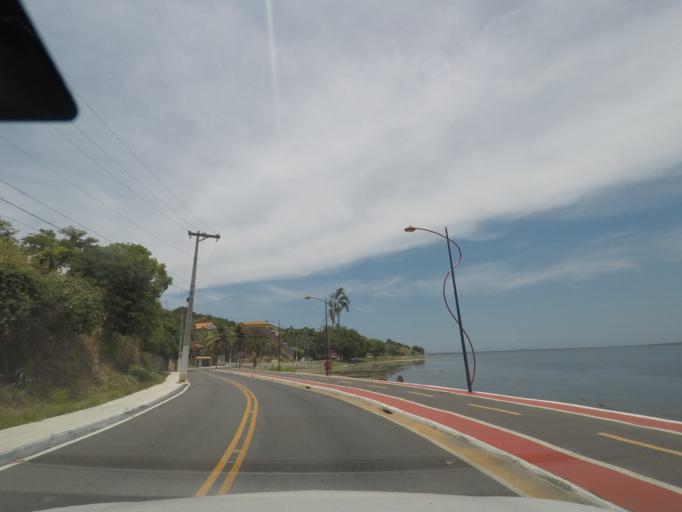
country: BR
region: Rio de Janeiro
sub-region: Marica
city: Marica
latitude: -22.9292
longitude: -42.8267
